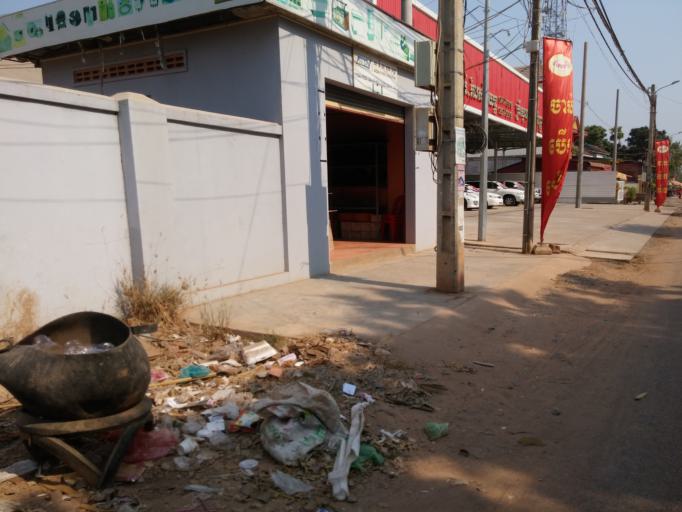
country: KH
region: Siem Reap
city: Siem Reap
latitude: 13.3689
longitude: 103.8488
